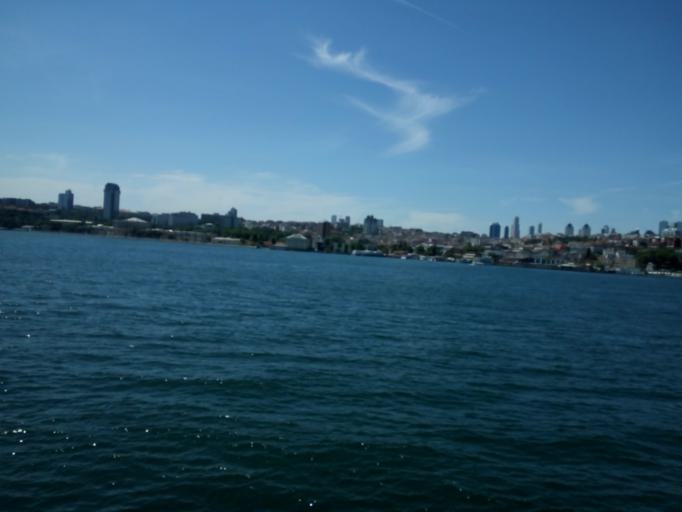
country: TR
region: Istanbul
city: UEskuedar
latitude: 41.0363
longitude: 29.0141
